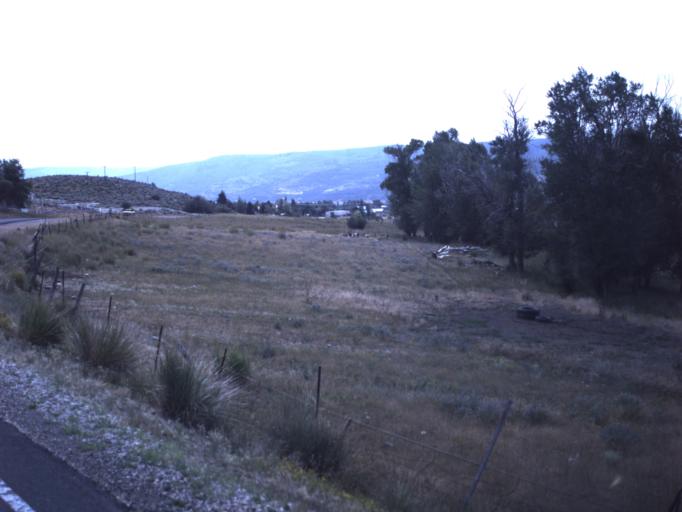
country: US
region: Utah
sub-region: Summit County
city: Francis
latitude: 40.6012
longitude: -111.2465
